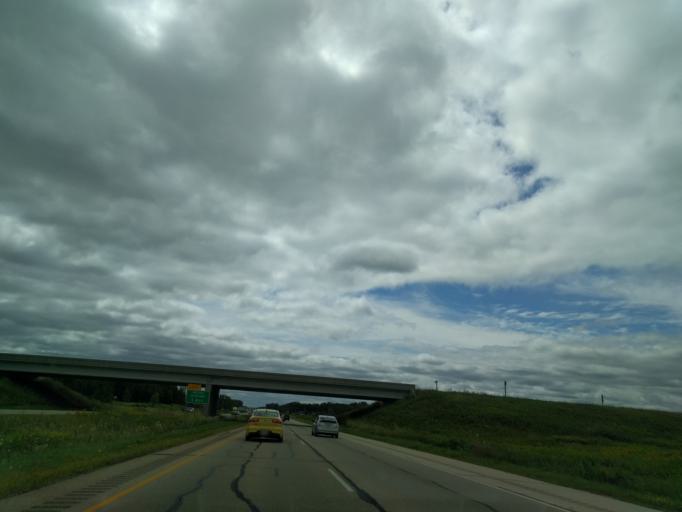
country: US
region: Wisconsin
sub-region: Brown County
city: Suamico
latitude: 44.7655
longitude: -88.0511
